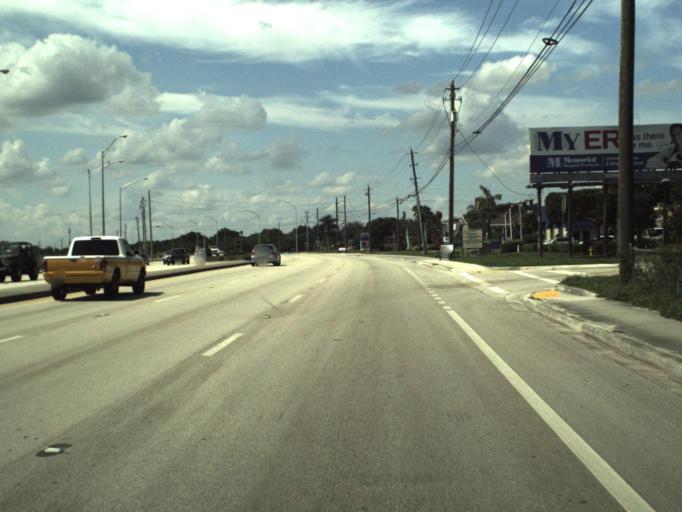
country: US
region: Florida
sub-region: Broward County
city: Davie
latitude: 26.0362
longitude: -80.2486
